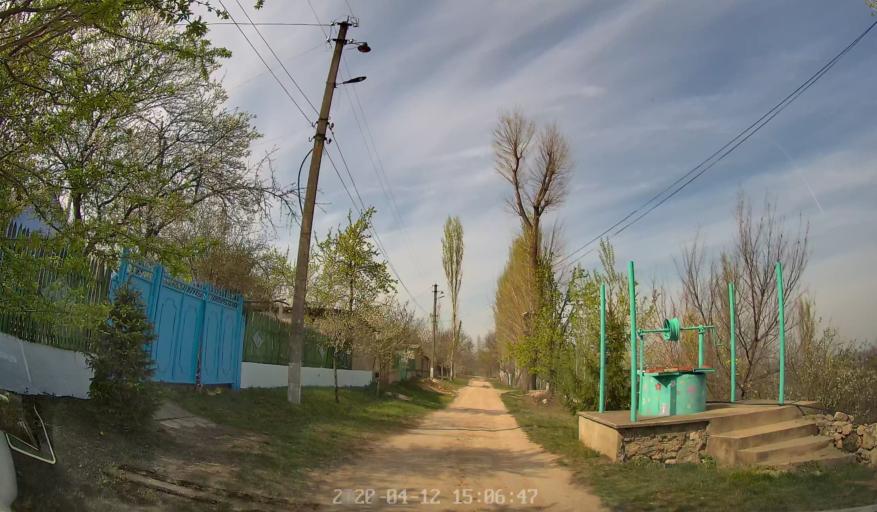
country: MD
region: Telenesti
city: Cocieri
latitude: 47.3151
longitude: 29.0726
